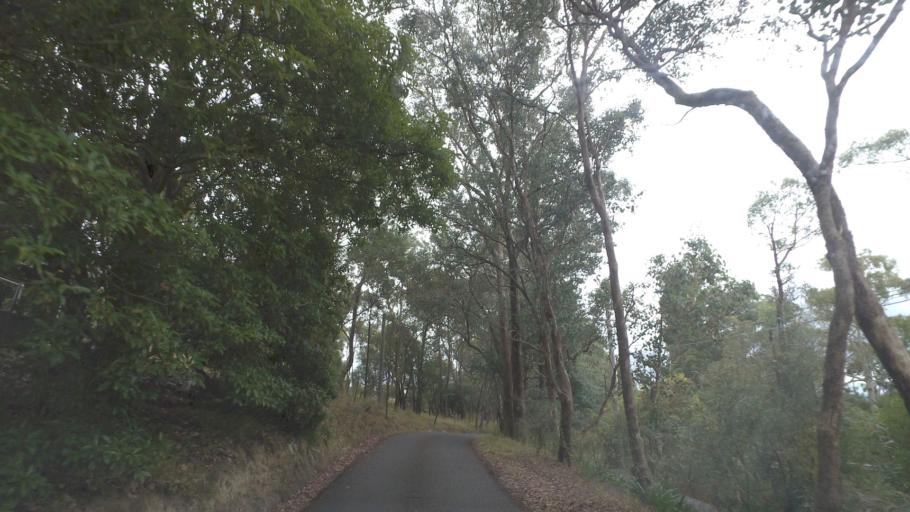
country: AU
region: Victoria
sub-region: Manningham
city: Park Orchards
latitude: -37.7581
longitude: 145.2149
